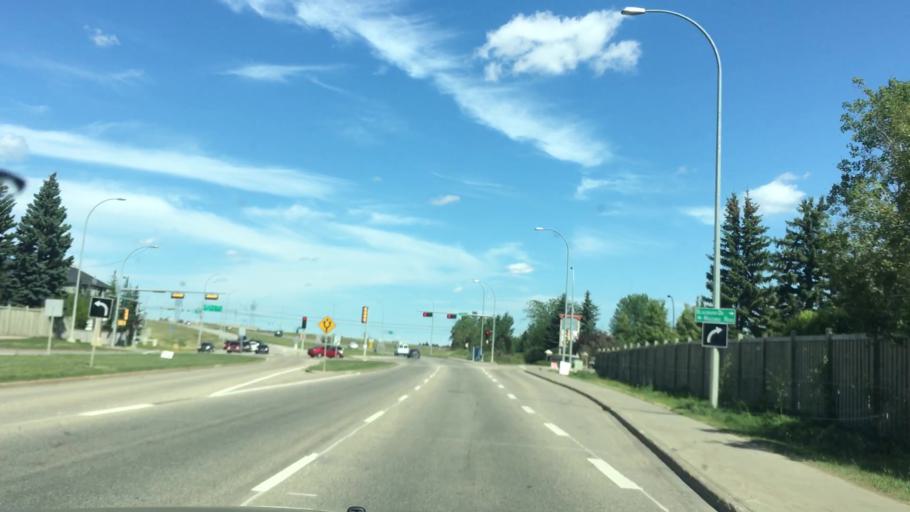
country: CA
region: Alberta
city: Beaumont
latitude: 53.4285
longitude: -113.5164
